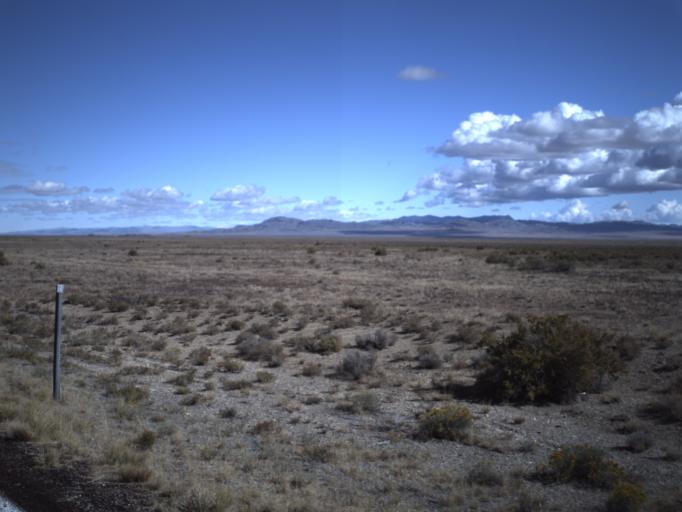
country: US
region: Nevada
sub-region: White Pine County
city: McGill
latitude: 38.9594
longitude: -114.0335
